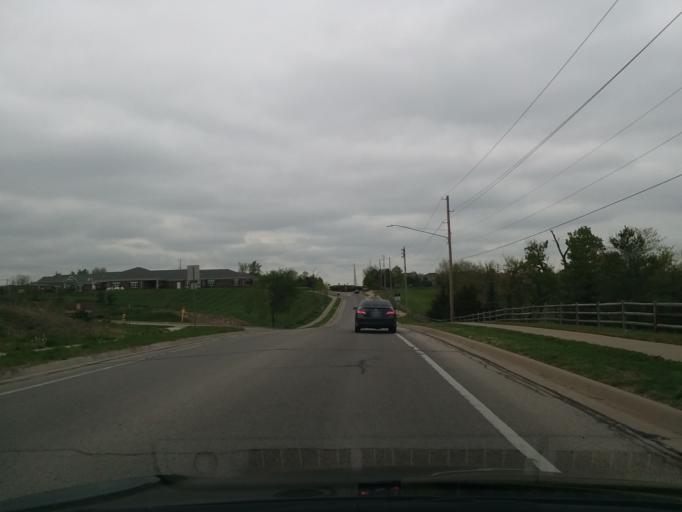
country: US
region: Kansas
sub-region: Douglas County
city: Lawrence
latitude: 38.9836
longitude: -95.2882
